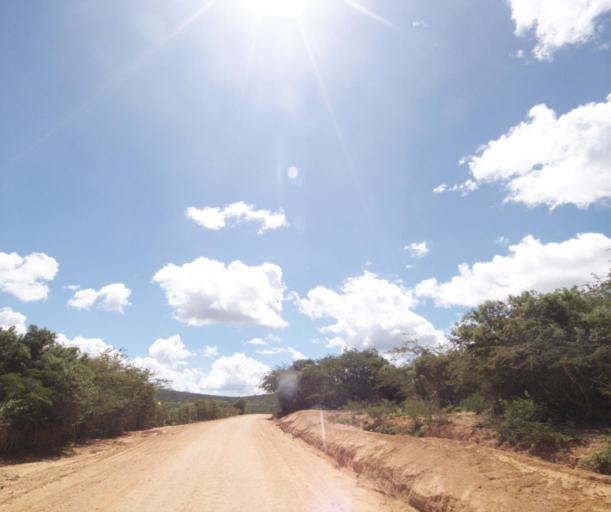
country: BR
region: Bahia
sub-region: Pocoes
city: Pocoes
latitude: -14.2997
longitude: -40.6535
